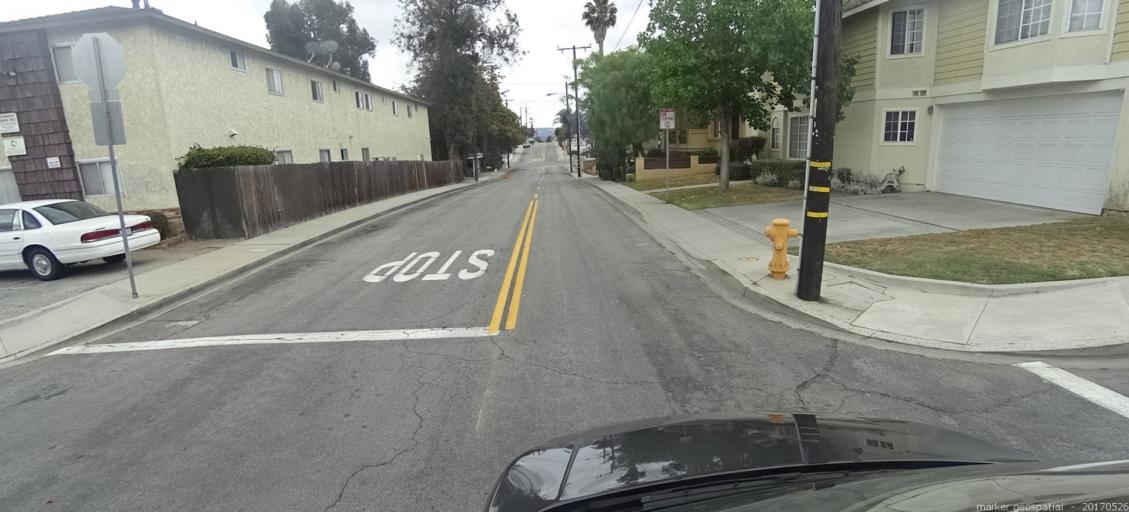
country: US
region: California
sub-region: Los Angeles County
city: Lawndale
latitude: 33.8757
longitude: -118.3622
